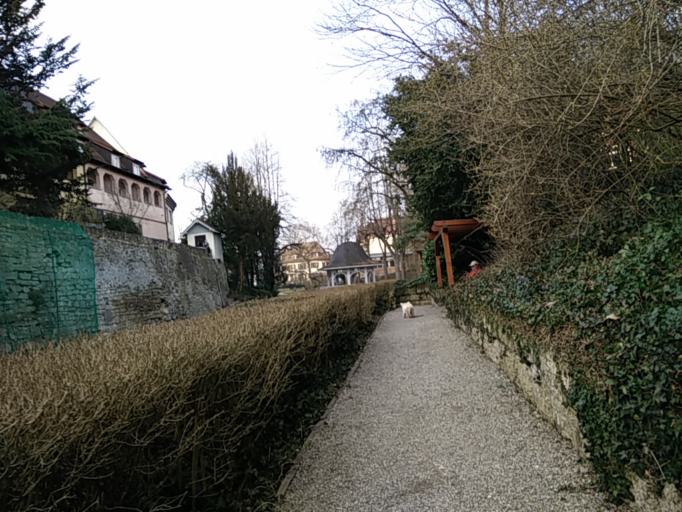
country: DE
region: Baden-Wuerttemberg
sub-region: Freiburg Region
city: Radolfzell am Bodensee
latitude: 47.7373
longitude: 8.9720
